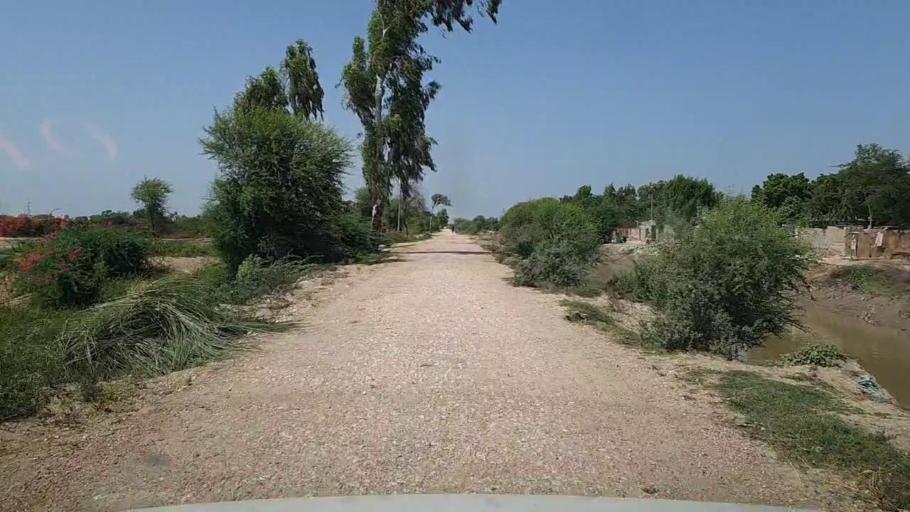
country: PK
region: Sindh
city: Kario
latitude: 24.6547
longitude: 68.5522
